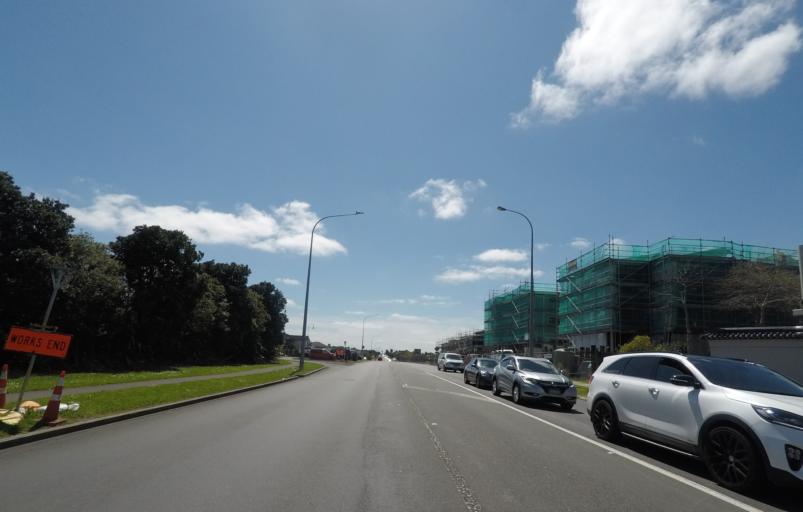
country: NZ
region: Auckland
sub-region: Auckland
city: Manukau City
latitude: -36.9569
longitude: 174.9088
